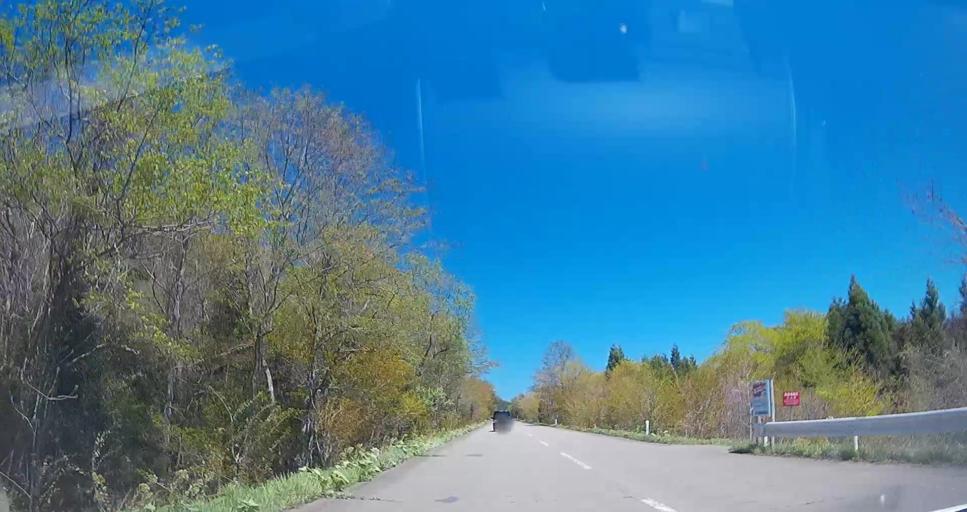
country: JP
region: Aomori
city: Mutsu
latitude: 41.3133
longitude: 141.3984
